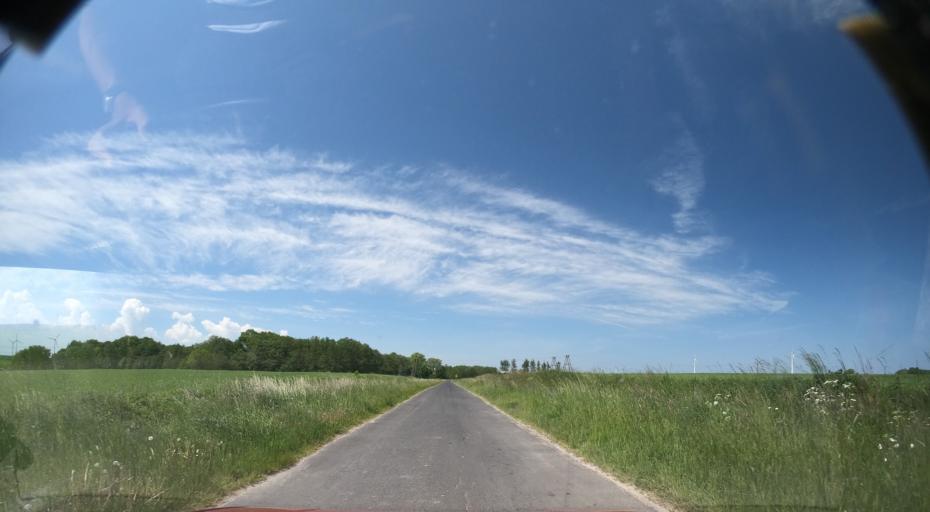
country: PL
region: West Pomeranian Voivodeship
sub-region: Powiat kolobrzeski
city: Dygowo
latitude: 54.1494
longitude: 15.7819
